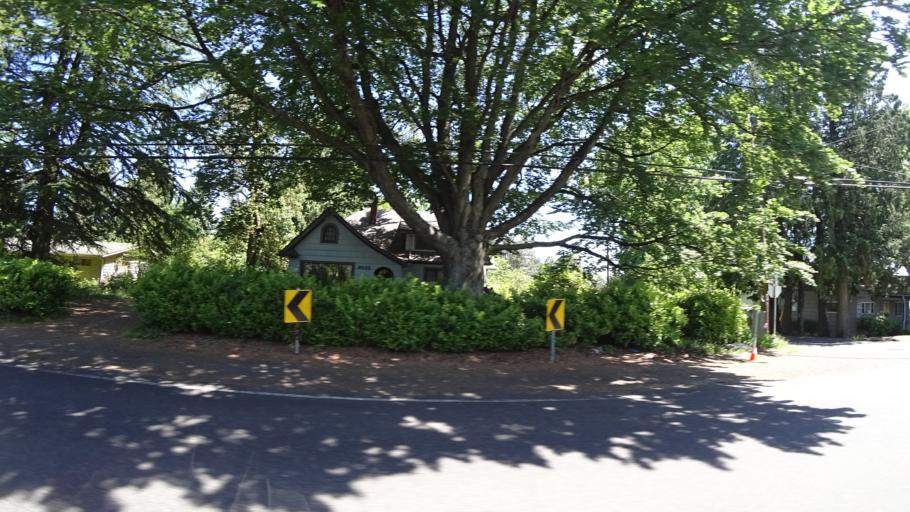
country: US
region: Oregon
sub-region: Washington County
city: Garden Home-Whitford
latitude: 45.4564
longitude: -122.7191
